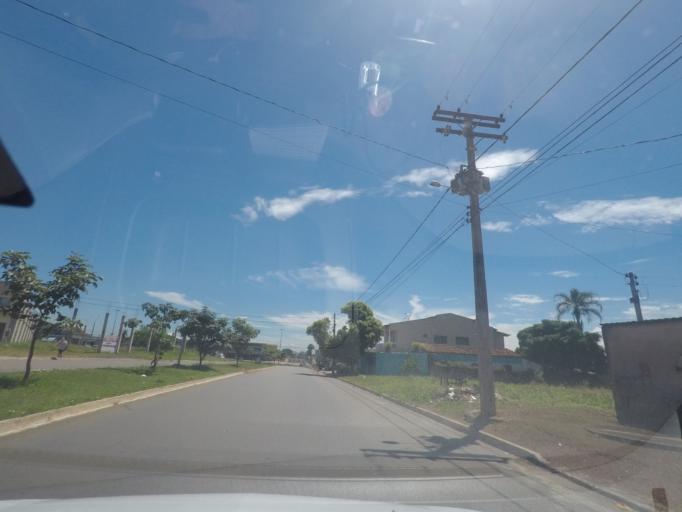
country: BR
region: Goias
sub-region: Aparecida De Goiania
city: Aparecida de Goiania
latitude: -16.7708
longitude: -49.3238
